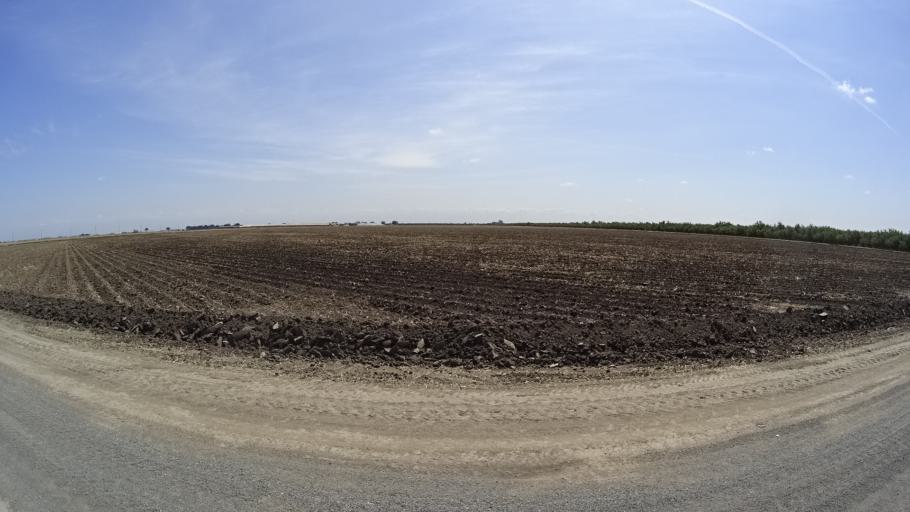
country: US
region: California
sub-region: Tulare County
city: Goshen
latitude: 36.2771
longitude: -119.4923
